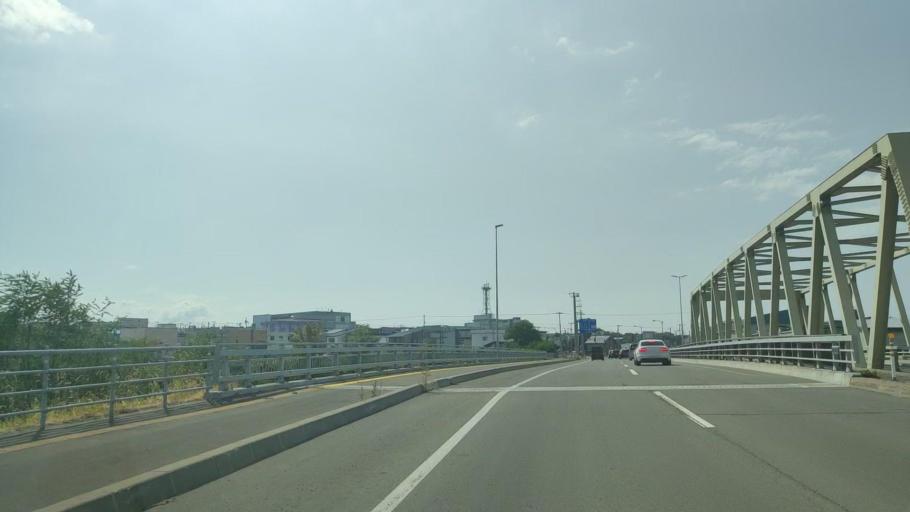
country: JP
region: Hokkaido
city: Rumoi
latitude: 43.9422
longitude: 141.6456
